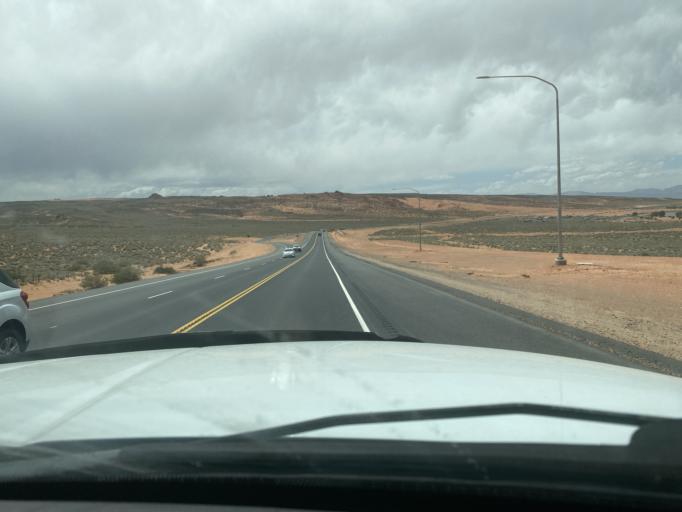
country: US
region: Utah
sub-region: Washington County
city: Hurricane
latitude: 37.1010
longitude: -113.3550
